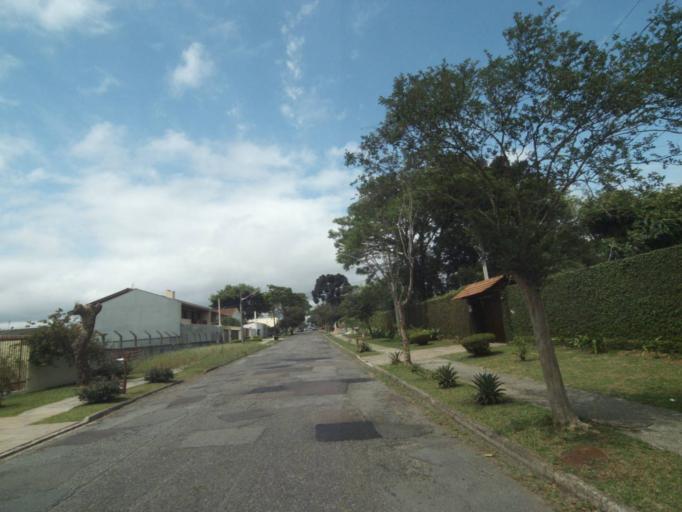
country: BR
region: Parana
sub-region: Pinhais
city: Pinhais
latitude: -25.4300
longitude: -49.2256
